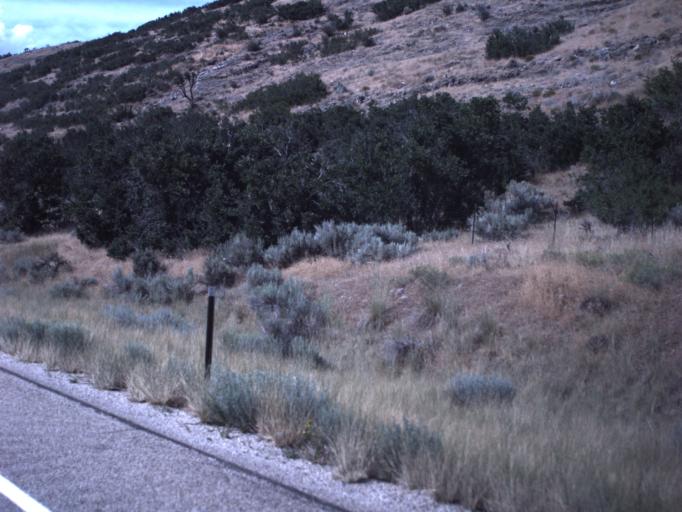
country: US
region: Utah
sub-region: Wasatch County
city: Heber
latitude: 40.4417
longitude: -111.3609
